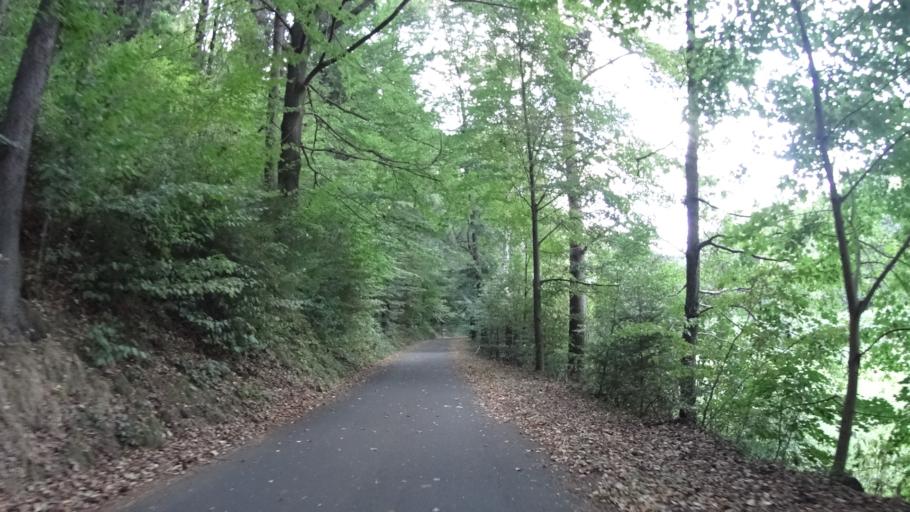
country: DE
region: Saxony
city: Ostritz
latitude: 50.9885
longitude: 14.9186
